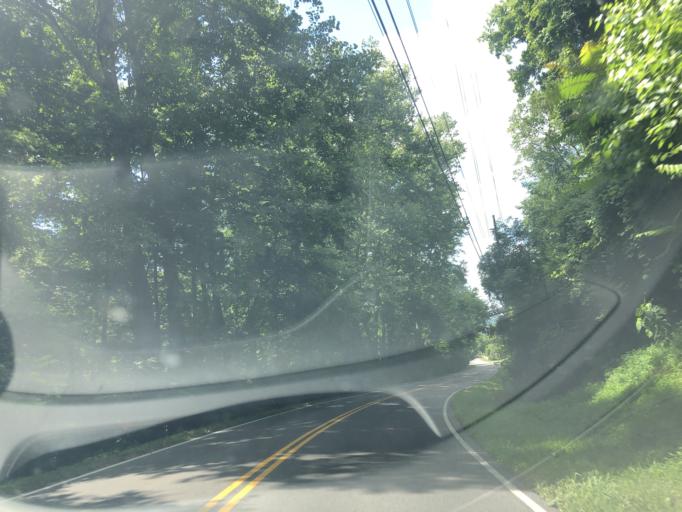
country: US
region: Tennessee
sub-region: Davidson County
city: Belle Meade
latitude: 36.0664
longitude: -86.9231
